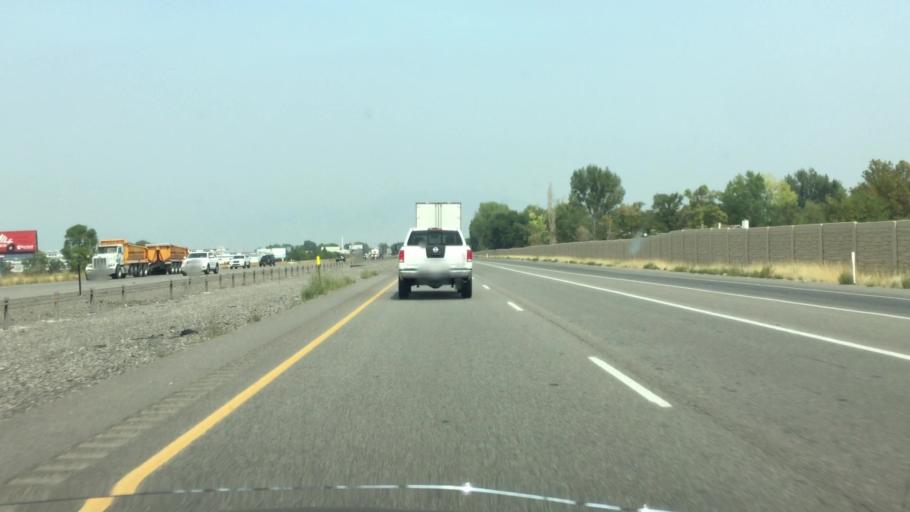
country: US
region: Utah
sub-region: Utah County
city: Payson
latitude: 40.0353
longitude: -111.7531
